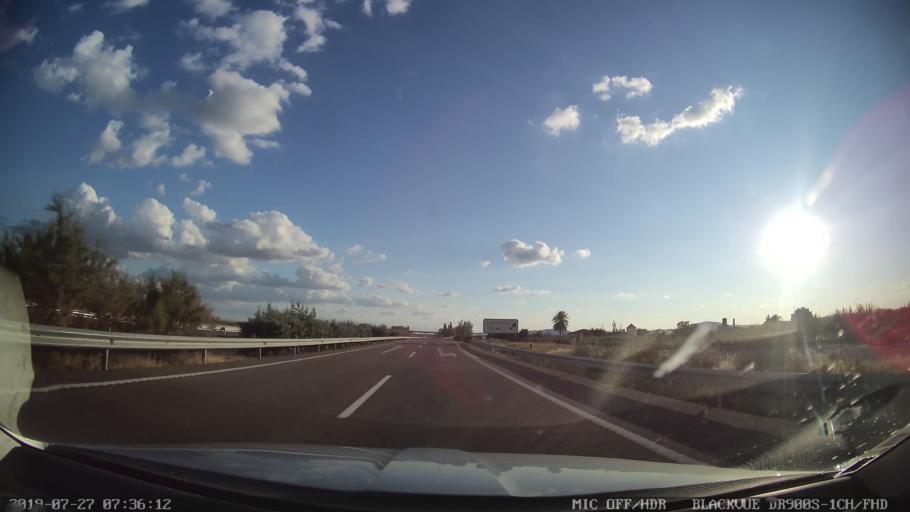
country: ES
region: Extremadura
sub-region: Provincia de Caceres
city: Almoharin
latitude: 39.1058
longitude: -5.9957
